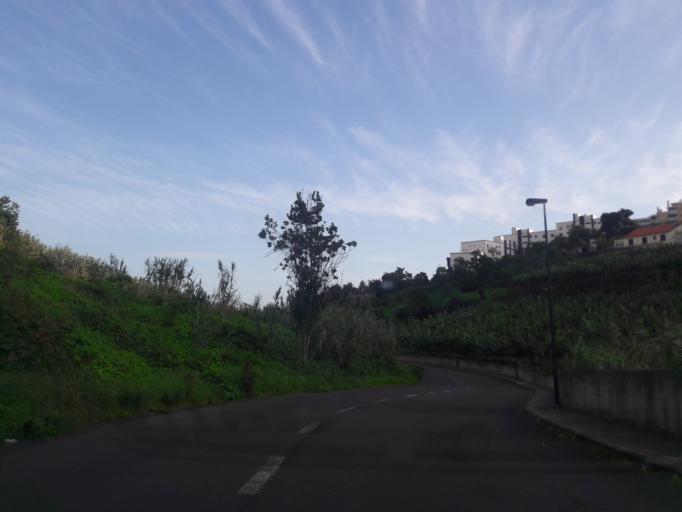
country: PT
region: Madeira
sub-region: Funchal
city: Nossa Senhora do Monte
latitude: 32.6580
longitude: -16.9316
